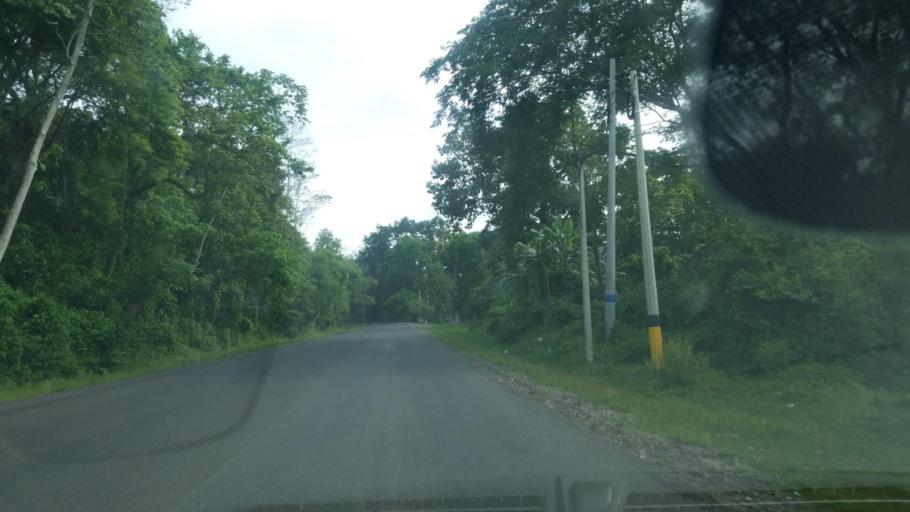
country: HN
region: Santa Barbara
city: Petoa
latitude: 15.2282
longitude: -88.2674
